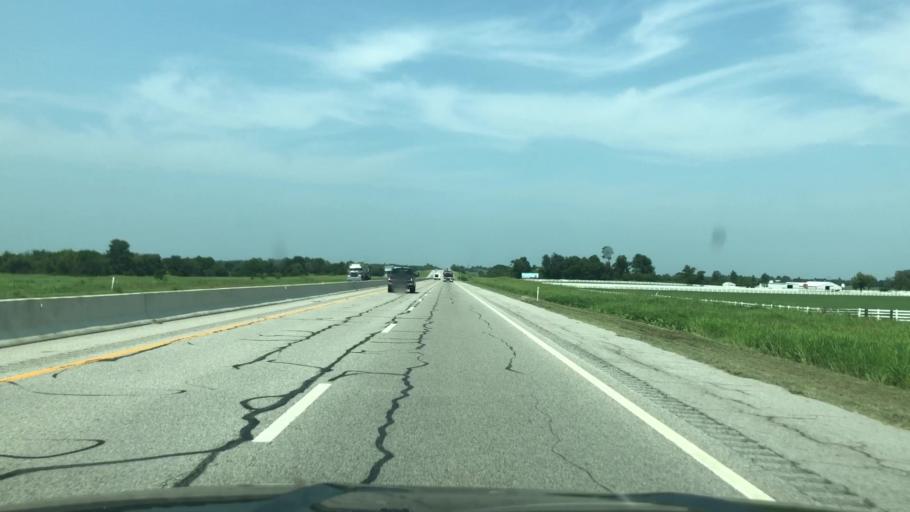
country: US
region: Oklahoma
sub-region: Ottawa County
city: Fairland
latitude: 36.8028
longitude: -94.8794
